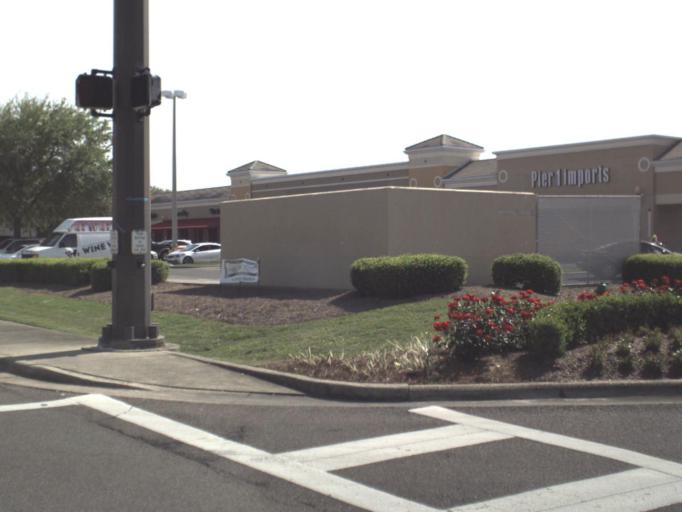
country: US
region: Florida
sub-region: Okaloosa County
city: Destin
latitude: 30.3911
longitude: -86.4268
